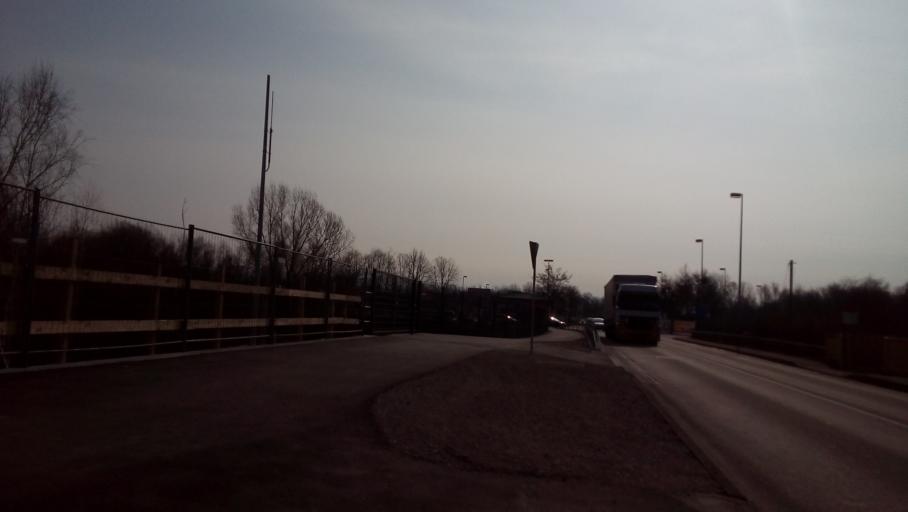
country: DE
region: Baden-Wuerttemberg
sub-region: Freiburg Region
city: Rheinau
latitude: 48.6819
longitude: 7.9201
